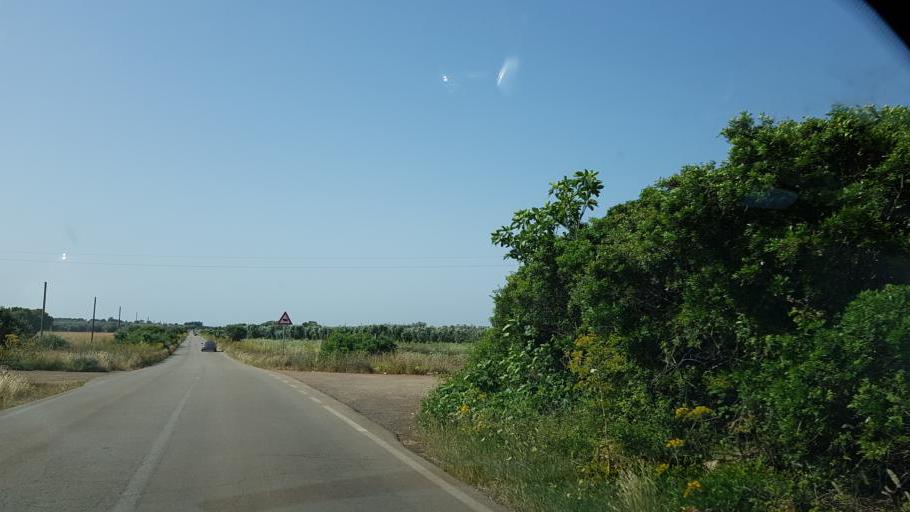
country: IT
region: Apulia
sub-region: Provincia di Brindisi
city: San Pancrazio Salentino
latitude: 40.3379
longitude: 17.8497
